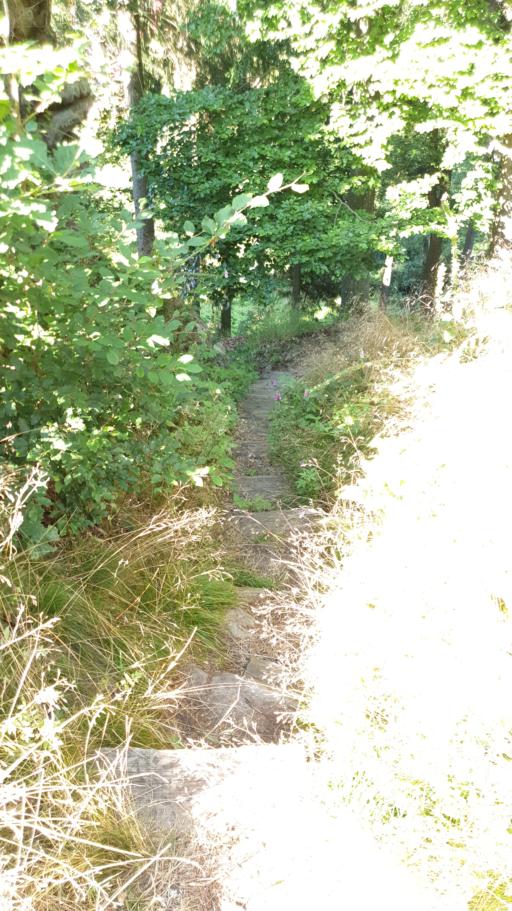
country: CZ
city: Kamenicky Senov
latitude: 50.7897
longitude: 14.4911
